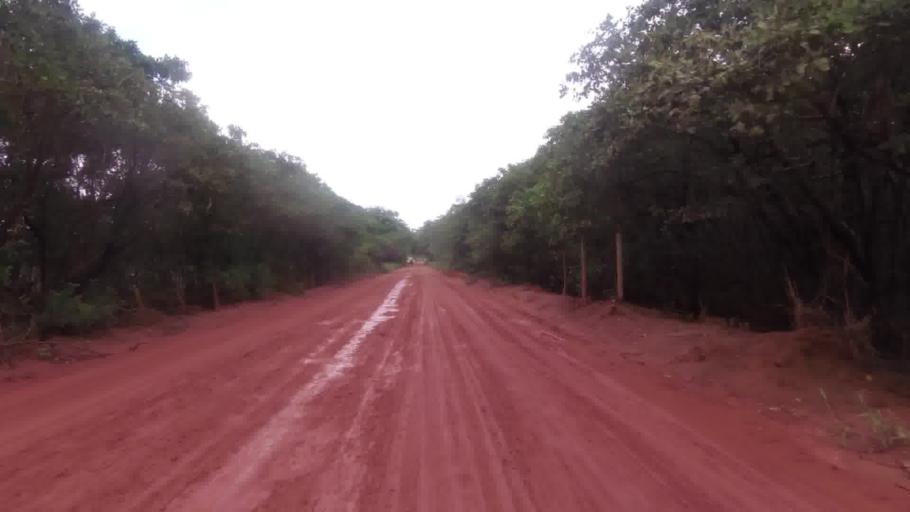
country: BR
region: Espirito Santo
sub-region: Piuma
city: Piuma
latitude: -20.7911
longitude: -40.6338
